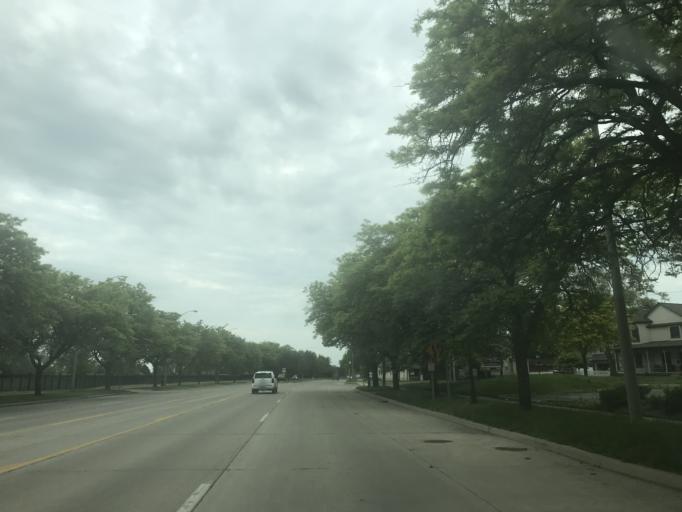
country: US
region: Michigan
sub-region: Wayne County
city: Wyandotte
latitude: 42.1965
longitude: -83.1524
